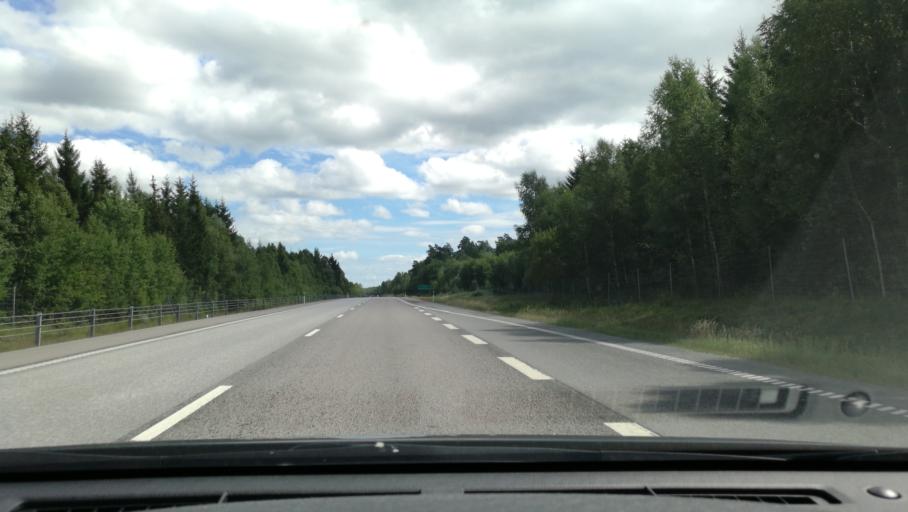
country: SE
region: Uppsala
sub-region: Enkopings Kommun
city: Dalby
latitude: 59.6165
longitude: 17.4002
